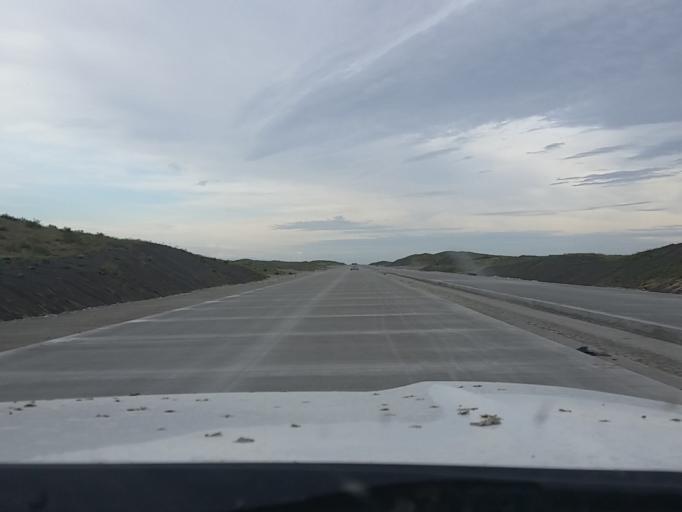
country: KZ
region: Almaty Oblysy
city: Zharkent
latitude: 44.1746
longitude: 80.3053
